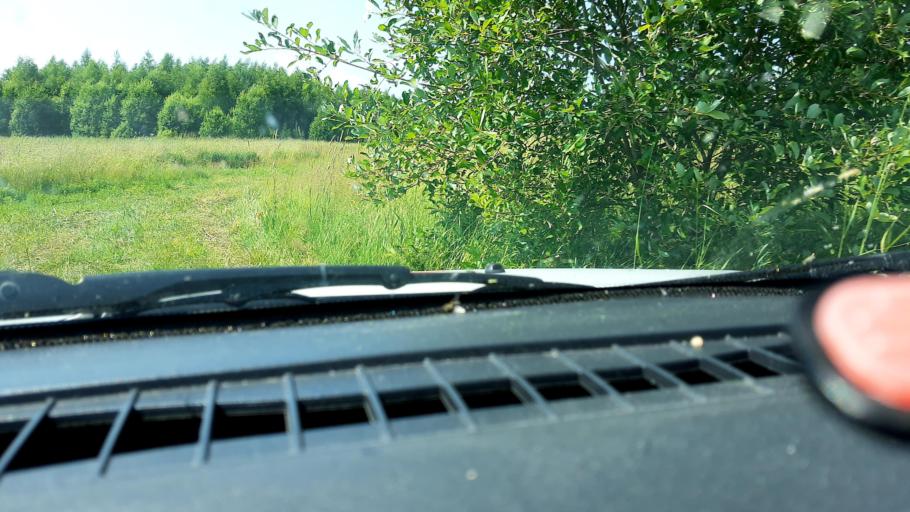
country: RU
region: Nizjnij Novgorod
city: Sharanga
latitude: 57.0460
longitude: 46.7295
